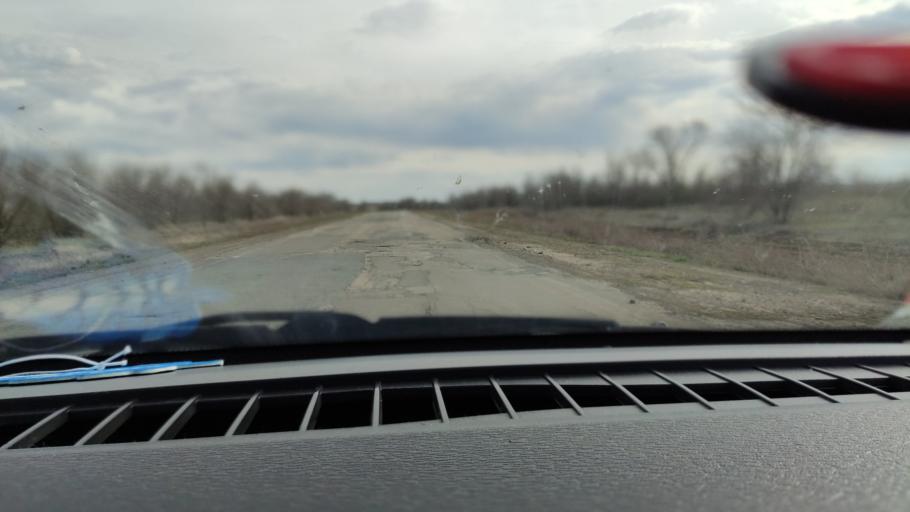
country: RU
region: Saratov
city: Rovnoye
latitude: 50.9633
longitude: 46.1171
